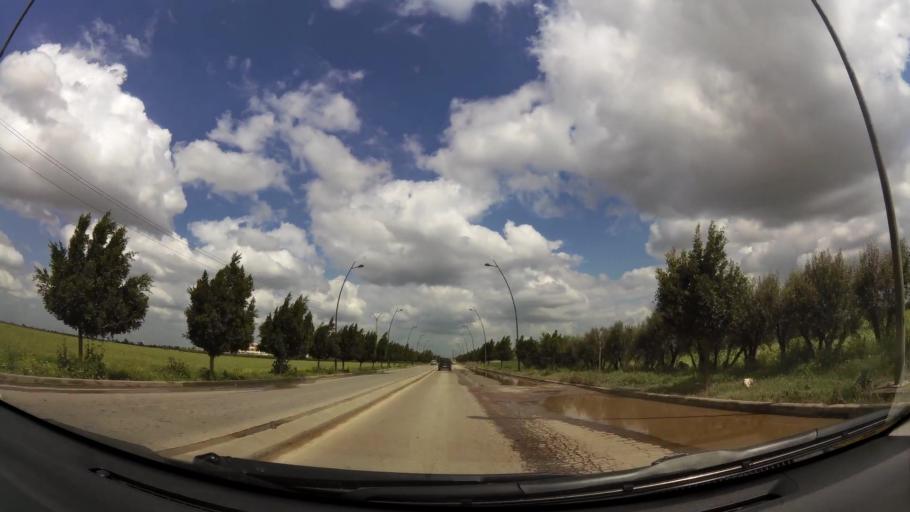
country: MA
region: Chaouia-Ouardigha
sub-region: Settat Province
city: Berrechid
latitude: 33.2612
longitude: -7.6113
